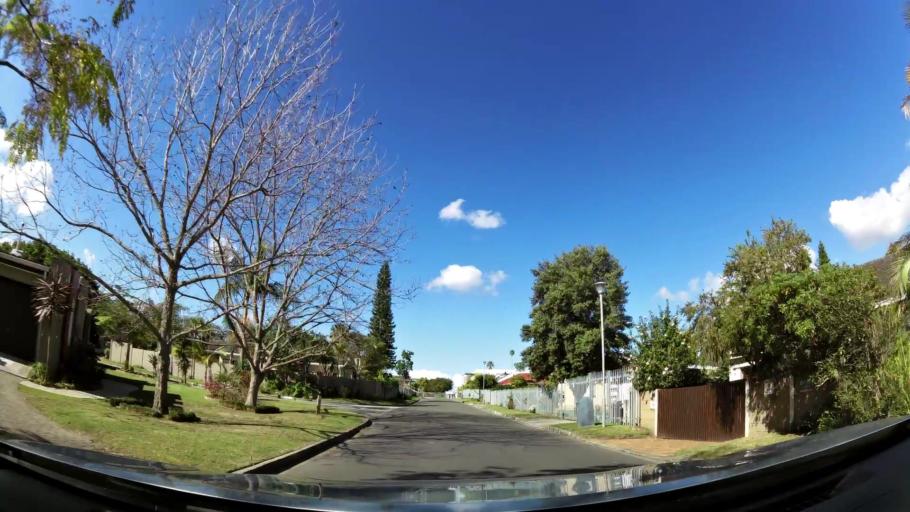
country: ZA
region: Western Cape
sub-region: Eden District Municipality
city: George
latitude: -33.9616
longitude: 22.4514
